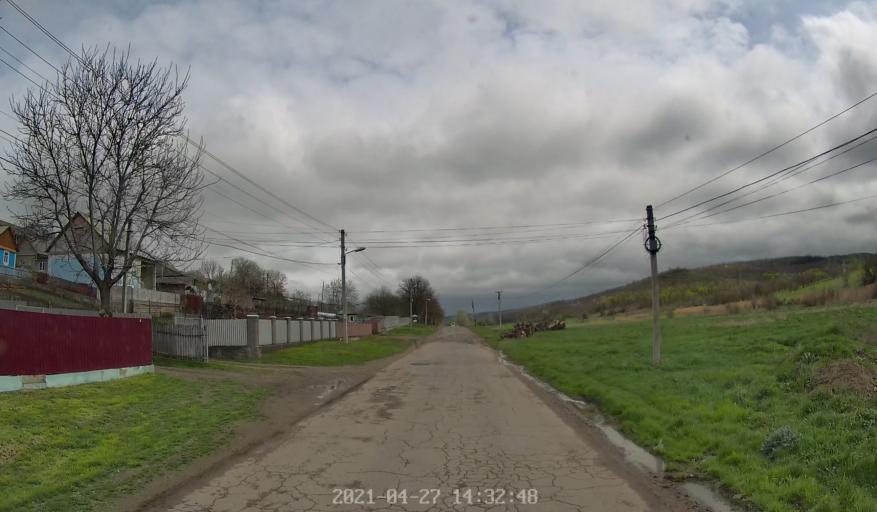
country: MD
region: Chisinau
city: Vadul lui Voda
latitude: 47.0619
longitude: 29.0152
